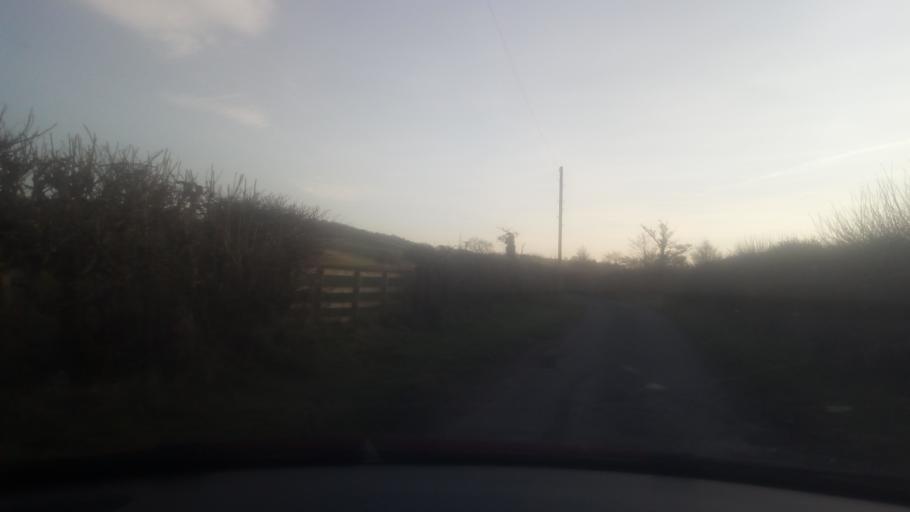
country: GB
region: Scotland
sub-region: The Scottish Borders
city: Jedburgh
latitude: 55.5078
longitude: -2.5375
